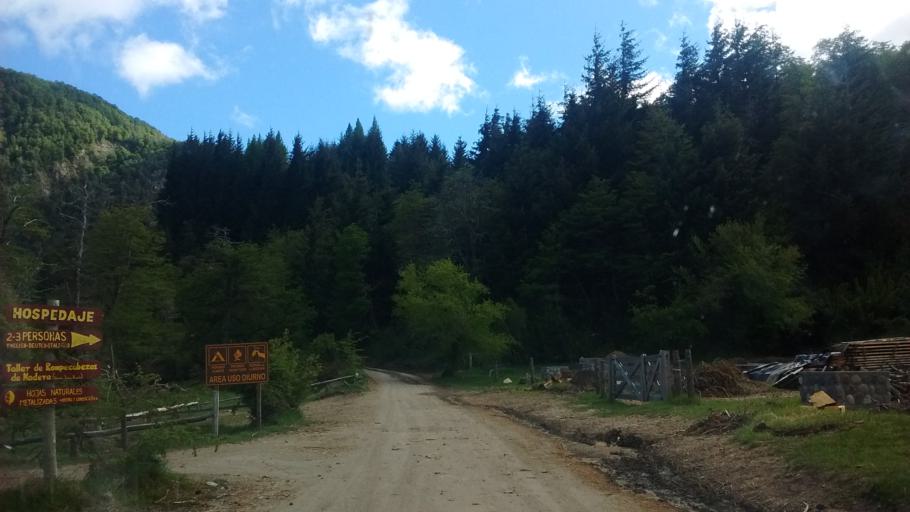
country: AR
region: Neuquen
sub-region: Departamento de Lacar
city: San Martin de los Andes
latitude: -40.3604
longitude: -71.4765
